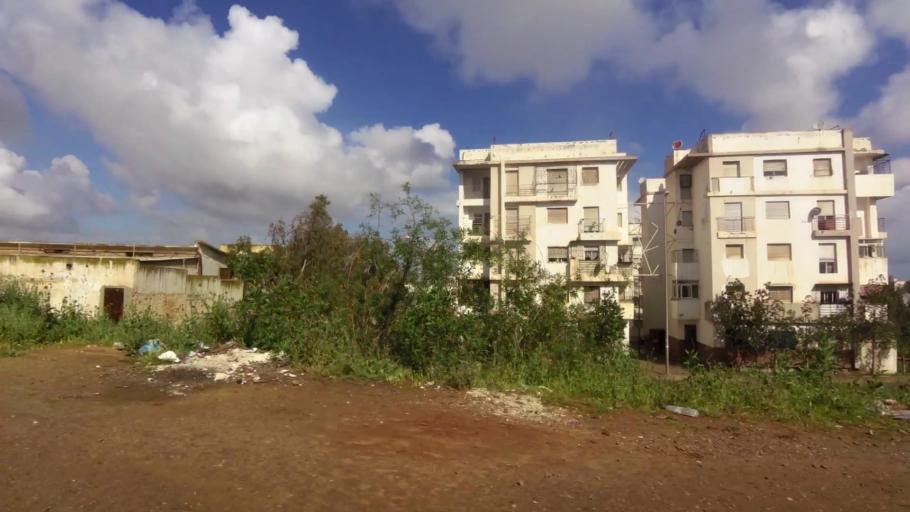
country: MA
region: Grand Casablanca
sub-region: Casablanca
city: Casablanca
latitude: 33.5348
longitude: -7.6845
